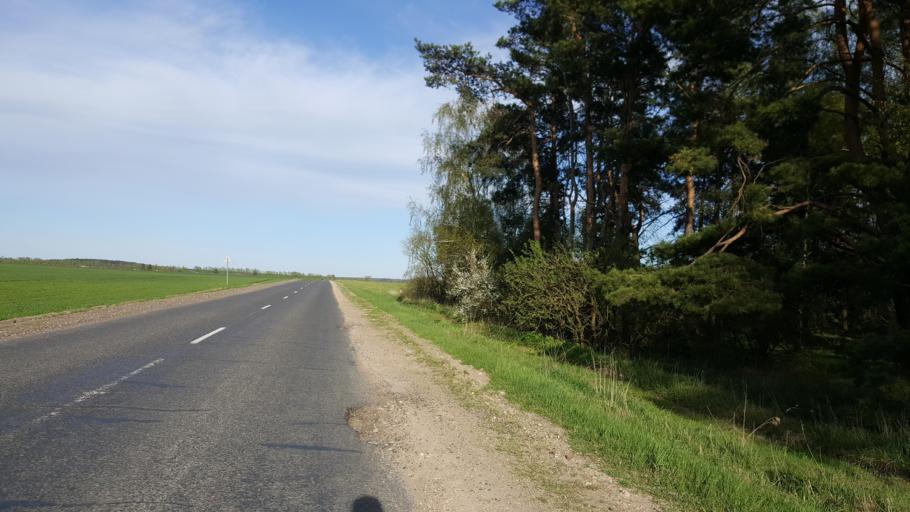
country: BY
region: Brest
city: Vysokaye
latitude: 52.4011
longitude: 23.5115
